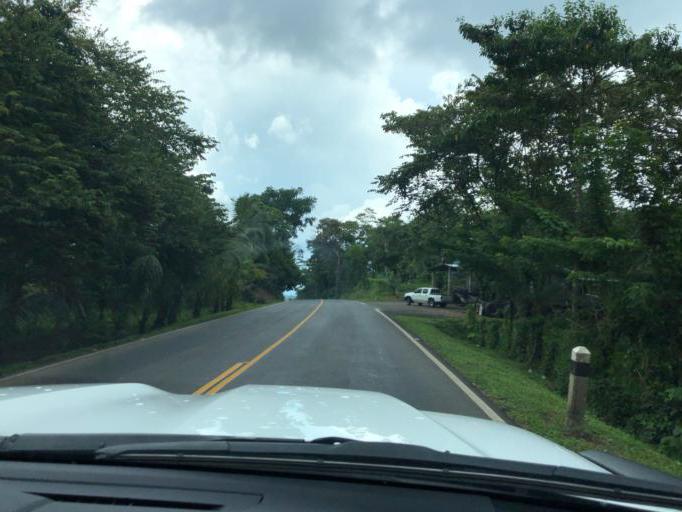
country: NI
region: Chontales
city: Villa Sandino
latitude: 11.9948
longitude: -84.7937
